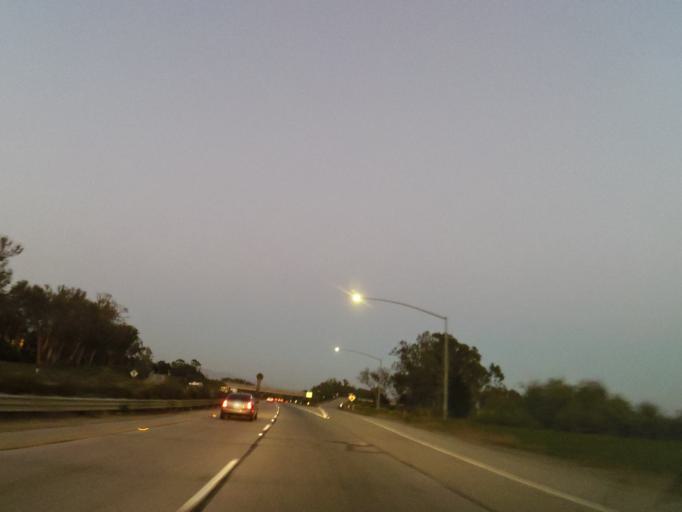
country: US
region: California
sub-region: Santa Barbara County
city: Summerland
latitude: 34.4167
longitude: -119.5862
